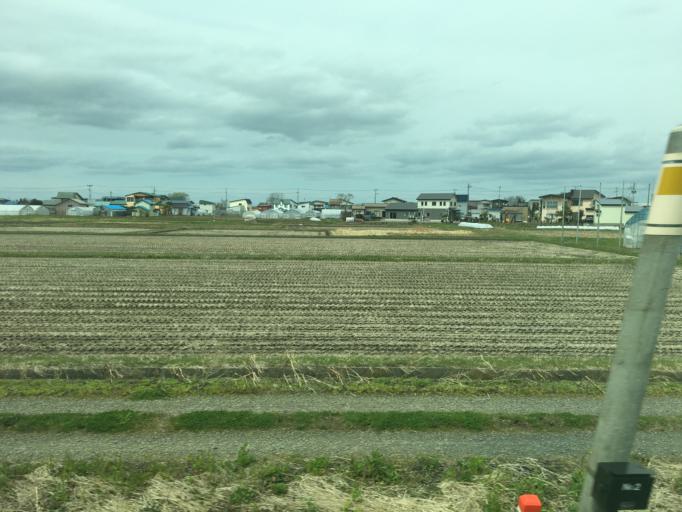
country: JP
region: Aomori
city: Shimokizukuri
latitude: 40.7931
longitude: 140.3738
